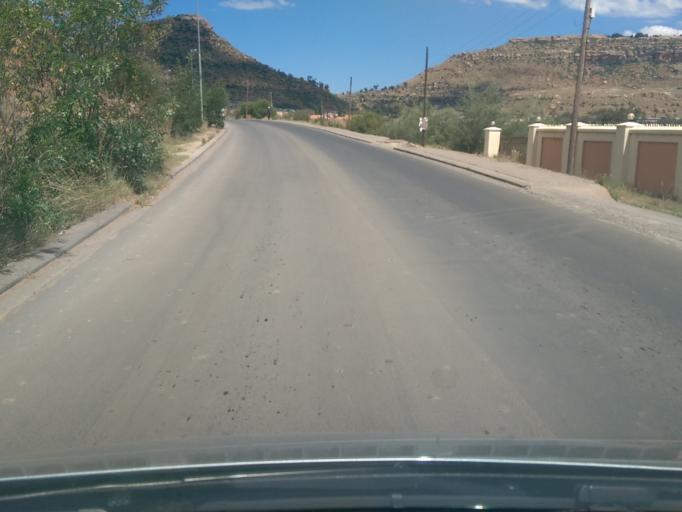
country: LS
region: Maseru
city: Maseru
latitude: -29.3227
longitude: 27.4832
